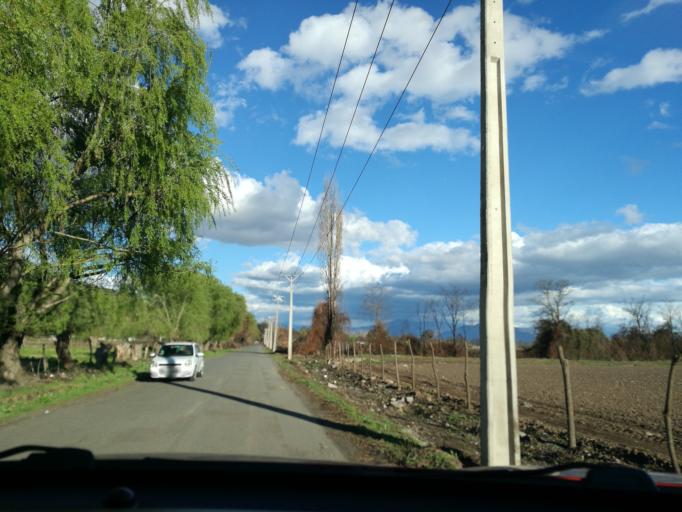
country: CL
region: O'Higgins
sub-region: Provincia de Cachapoal
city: Graneros
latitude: -34.0977
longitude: -70.8152
